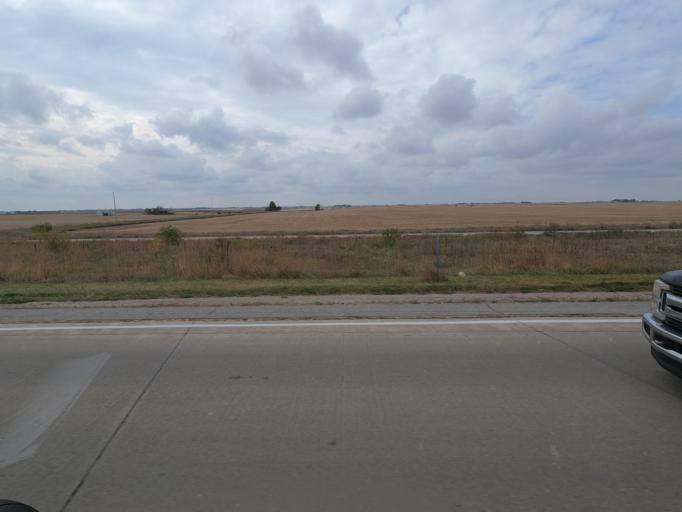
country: US
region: Iowa
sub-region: Jasper County
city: Monroe
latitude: 41.5378
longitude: -93.1304
